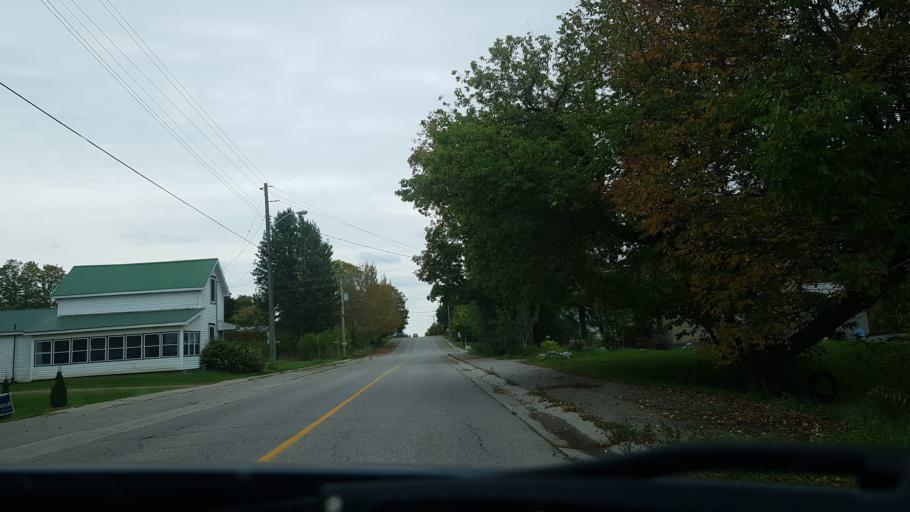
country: CA
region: Ontario
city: Orillia
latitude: 44.5971
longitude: -78.9401
